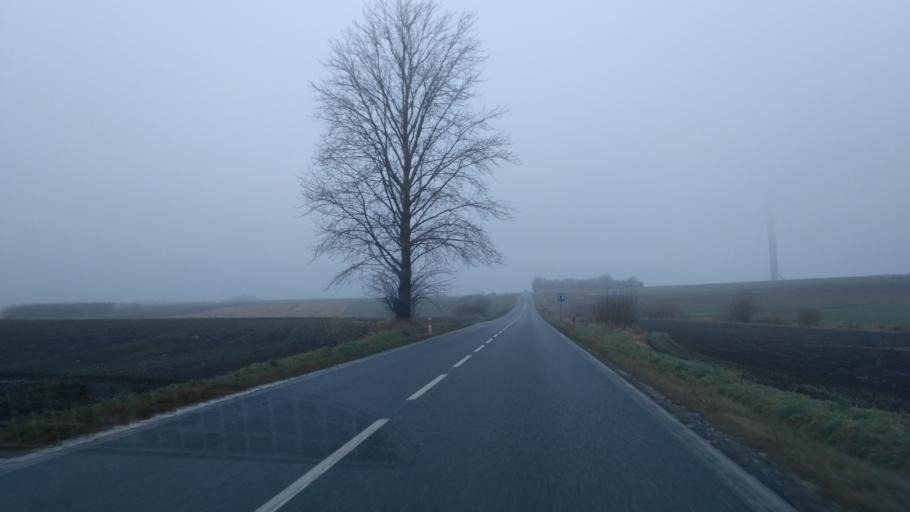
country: PL
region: Subcarpathian Voivodeship
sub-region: Powiat lancucki
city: Sonina
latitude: 50.0474
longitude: 22.2948
